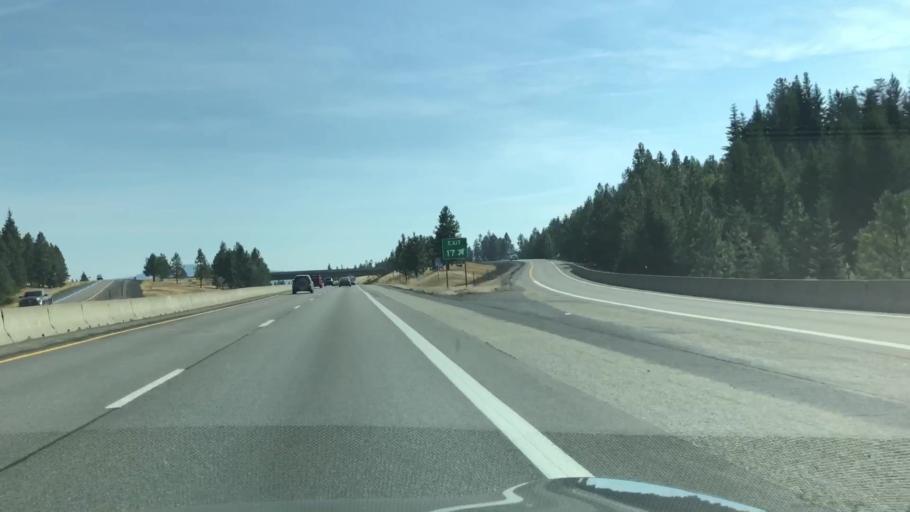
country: US
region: Idaho
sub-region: Kootenai County
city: Coeur d'Alene
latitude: 47.6585
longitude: -116.7281
